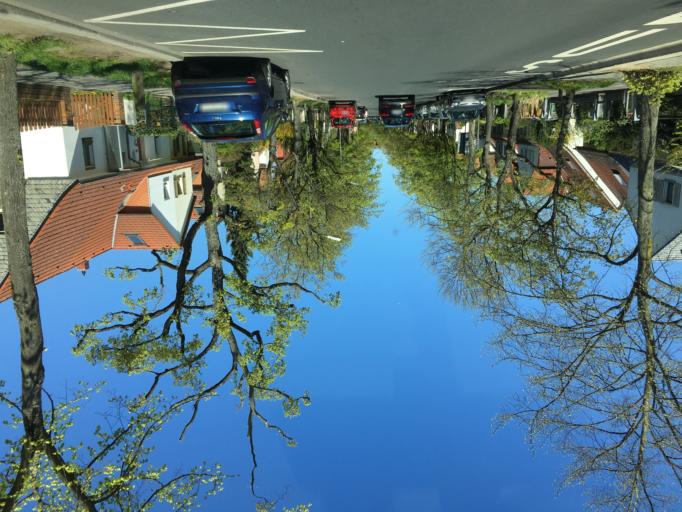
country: DE
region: Hesse
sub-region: Regierungsbezirk Darmstadt
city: Offenbach
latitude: 50.0900
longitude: 8.7627
